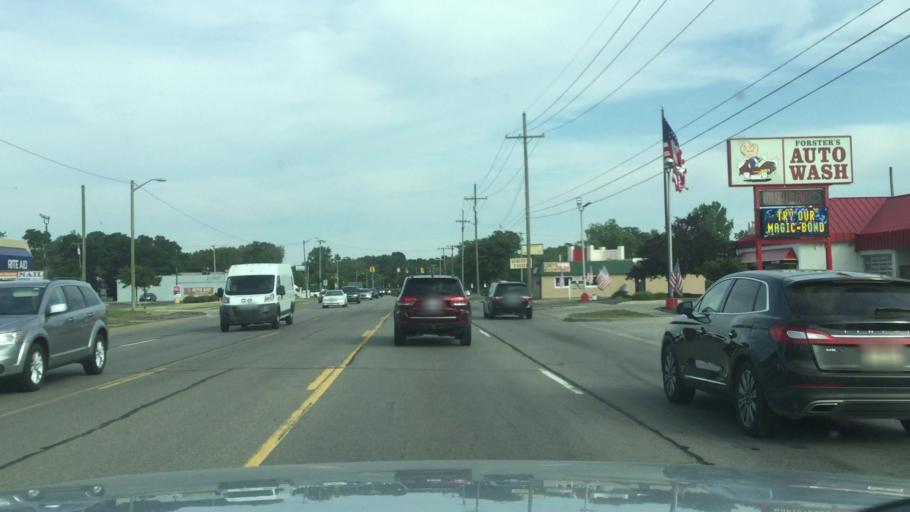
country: US
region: Michigan
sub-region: Oakland County
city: Waterford
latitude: 42.6829
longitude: -83.3760
